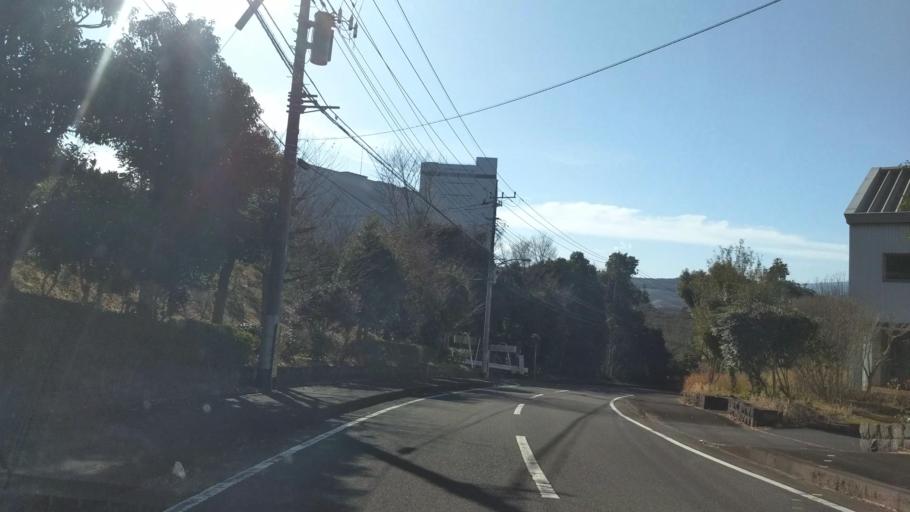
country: JP
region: Kanagawa
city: Hadano
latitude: 35.3430
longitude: 139.2248
